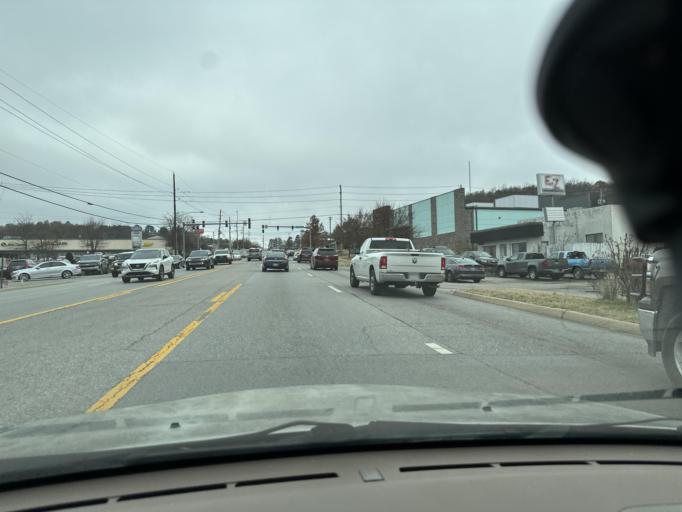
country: US
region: Arkansas
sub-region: Washington County
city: Fayetteville
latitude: 36.0853
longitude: -94.1554
